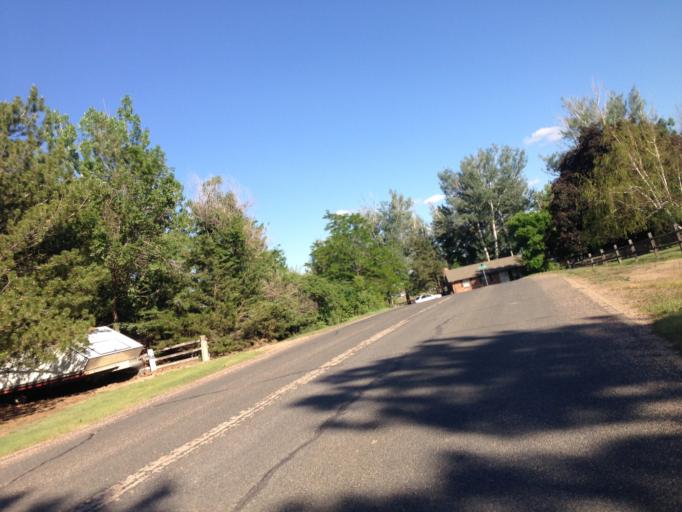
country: US
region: Colorado
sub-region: Boulder County
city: Lafayette
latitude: 40.0186
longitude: -105.1051
